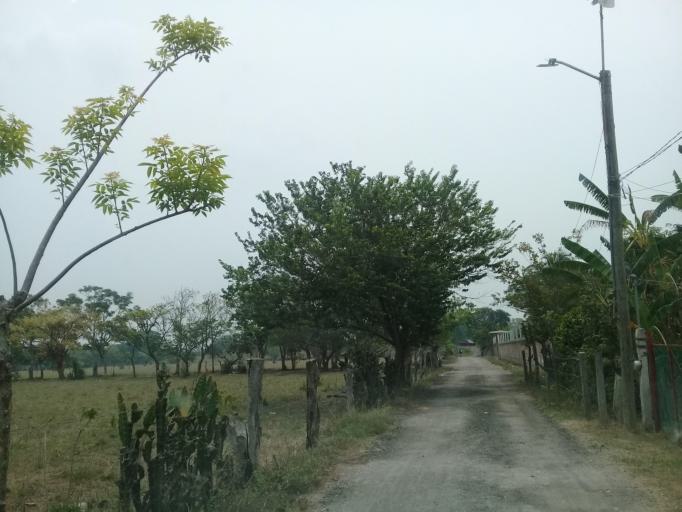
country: MX
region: Veracruz
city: Jamapa
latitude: 18.9554
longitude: -96.1965
